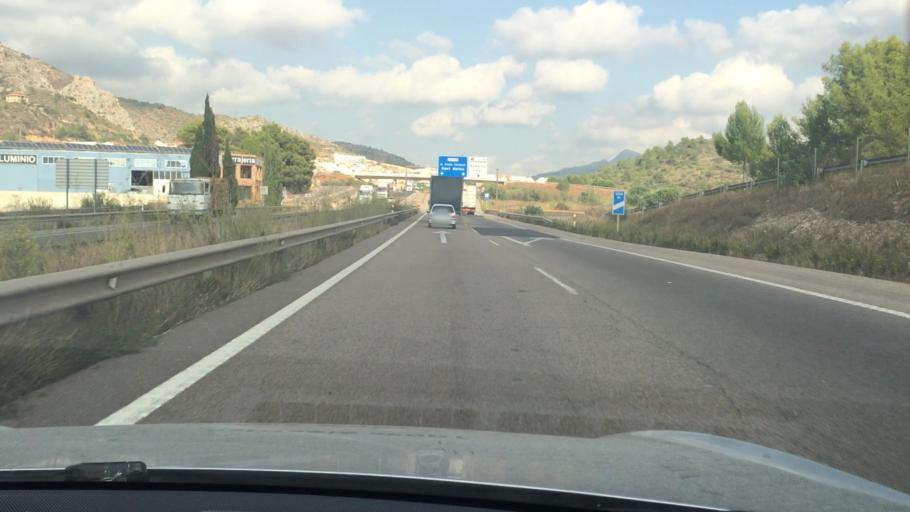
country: ES
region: Valencia
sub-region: Provincia de Castello
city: Borriol
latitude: 40.0328
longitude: -0.0814
